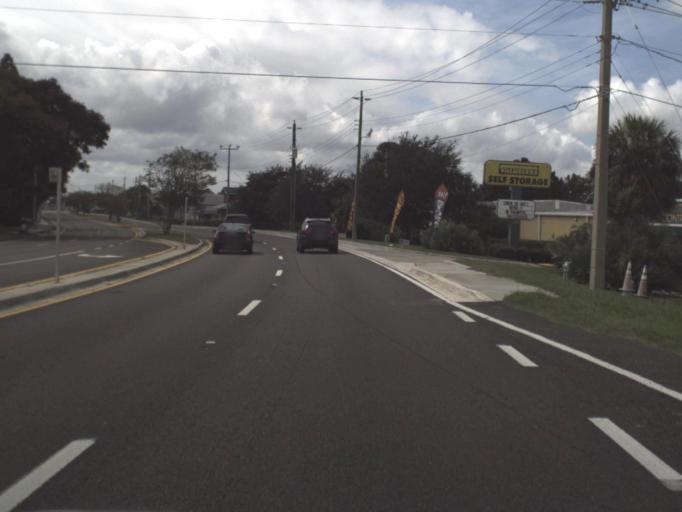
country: US
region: Florida
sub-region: Manatee County
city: Palmetto
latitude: 27.5325
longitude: -82.5728
